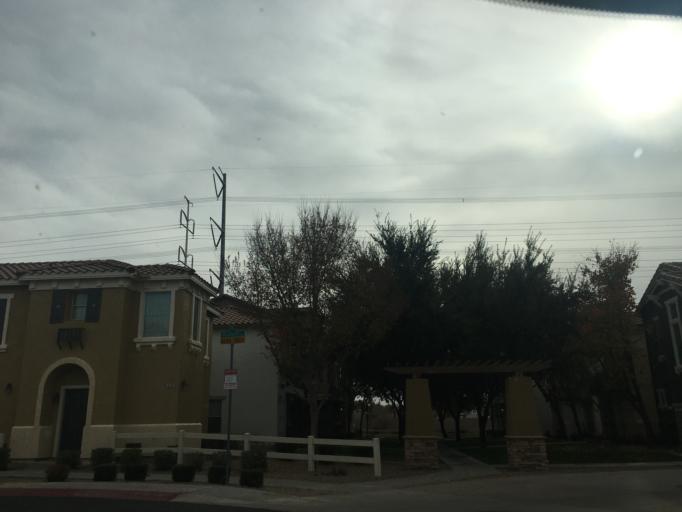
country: US
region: Arizona
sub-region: Maricopa County
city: Gilbert
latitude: 33.3582
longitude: -111.7932
